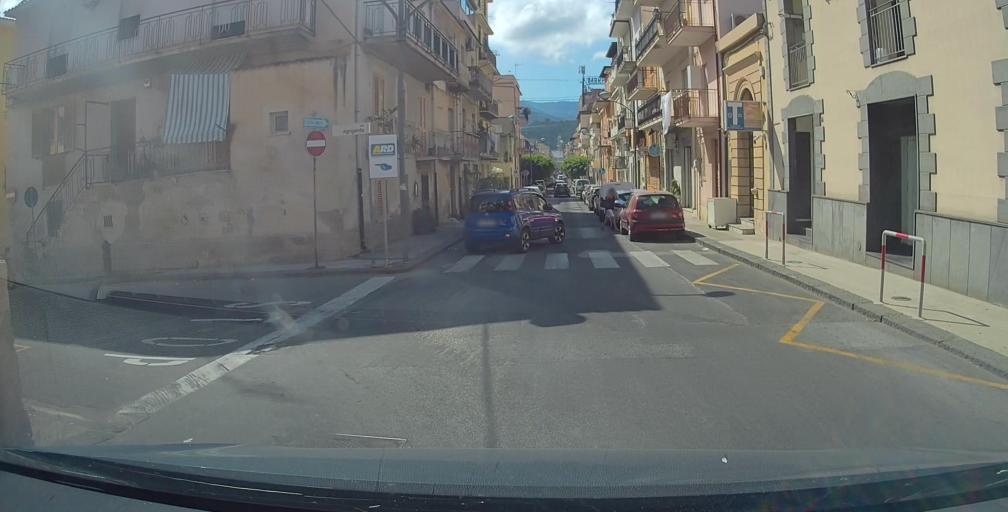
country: IT
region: Sicily
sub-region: Messina
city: Patti
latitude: 38.1512
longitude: 14.9714
